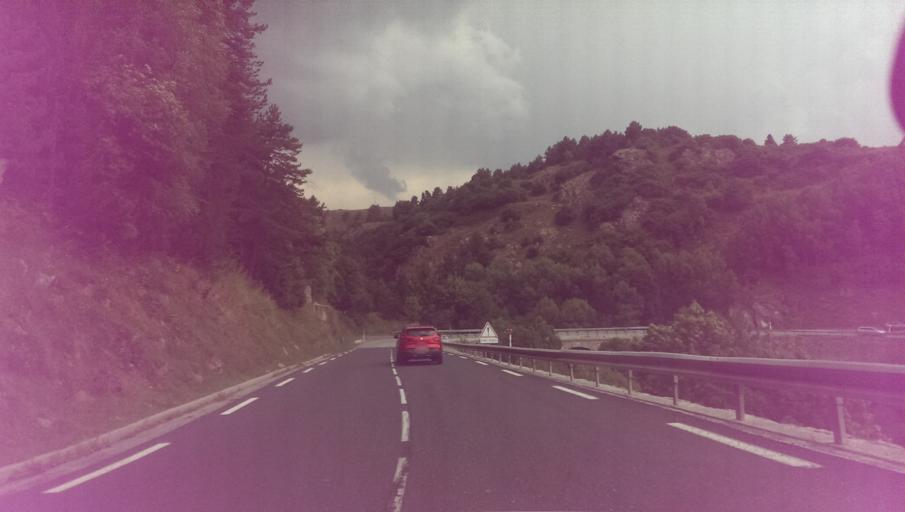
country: ES
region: Catalonia
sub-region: Provincia de Girona
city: Llivia
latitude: 42.5110
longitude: 2.1232
